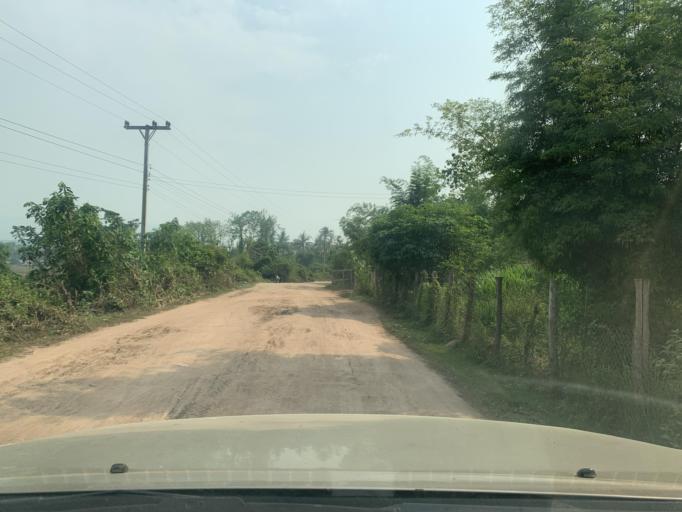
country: LA
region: Louangphabang
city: Louangphabang
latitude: 19.9092
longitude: 102.1338
